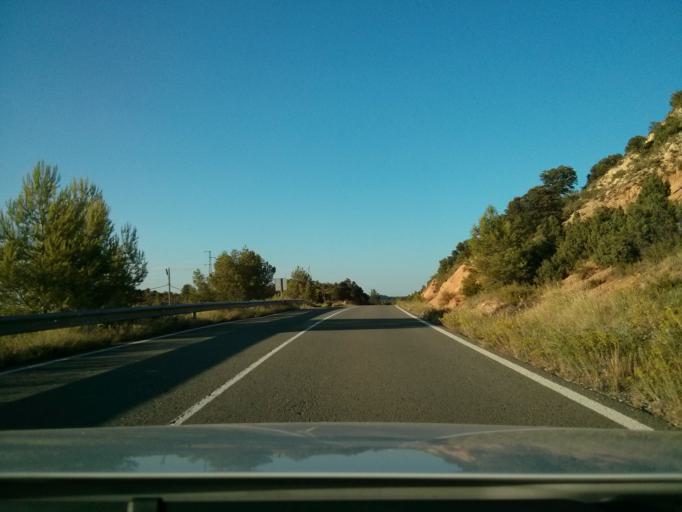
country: ES
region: Castille-La Mancha
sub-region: Provincia de Guadalajara
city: Chillaron del Rey
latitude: 40.6068
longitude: -2.6950
